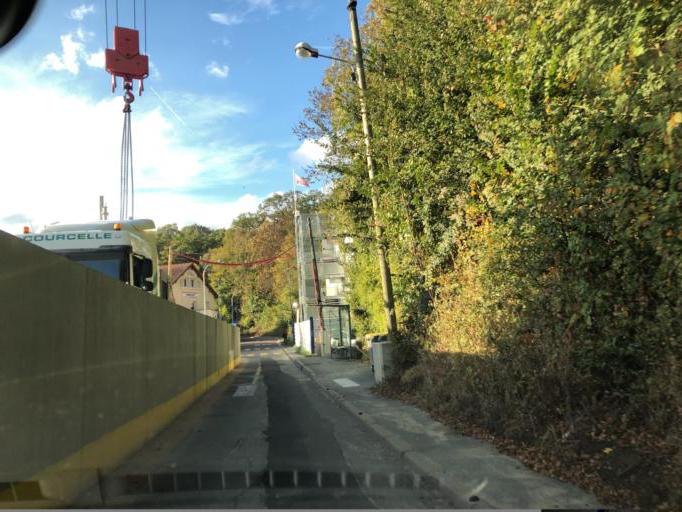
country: FR
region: Ile-de-France
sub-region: Departement des Hauts-de-Seine
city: Chaville
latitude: 48.7991
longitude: 2.1979
